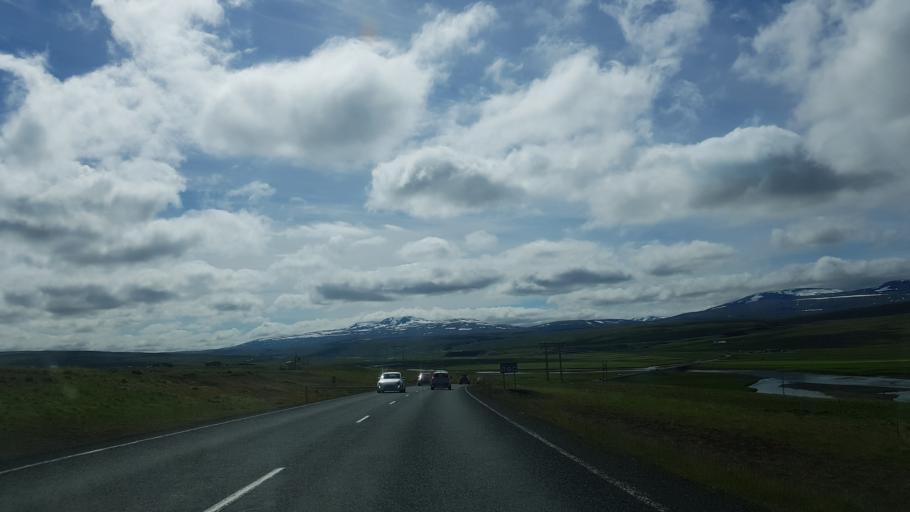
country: IS
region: West
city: Borgarnes
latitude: 65.1536
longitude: -21.0603
